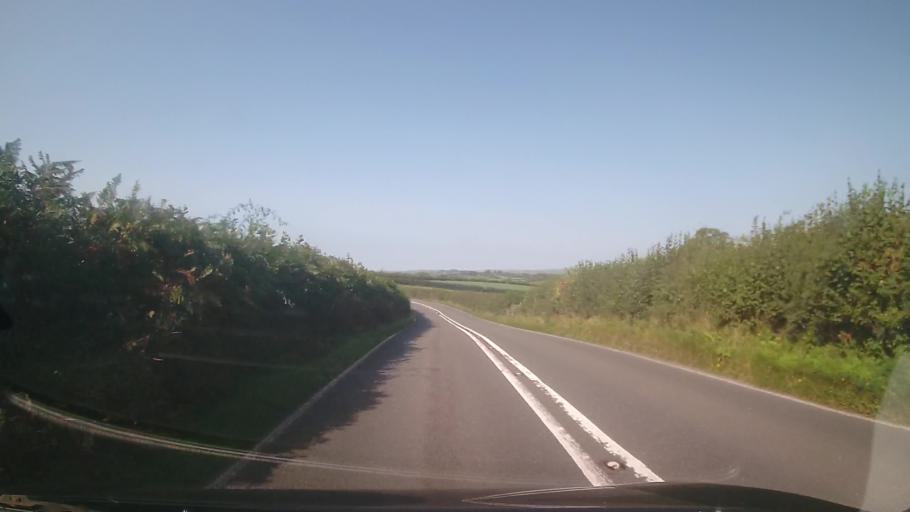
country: GB
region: Wales
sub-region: Sir Powys
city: Builth Wells
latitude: 52.1502
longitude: -3.4398
